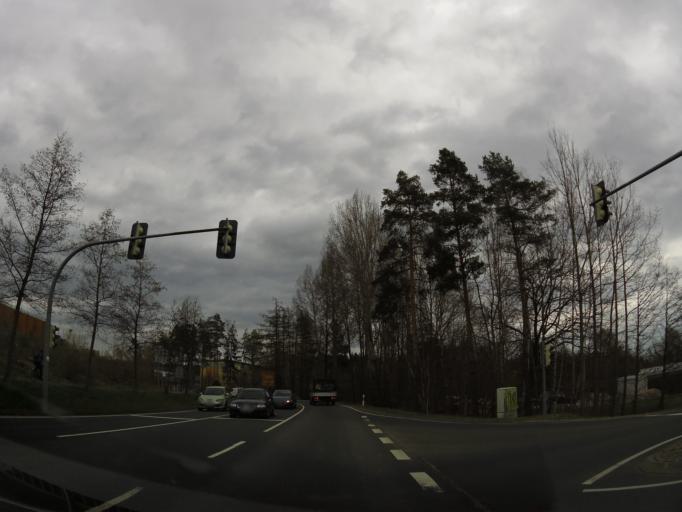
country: DE
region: Thuringia
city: Neuhaus
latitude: 50.6904
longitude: 10.9469
